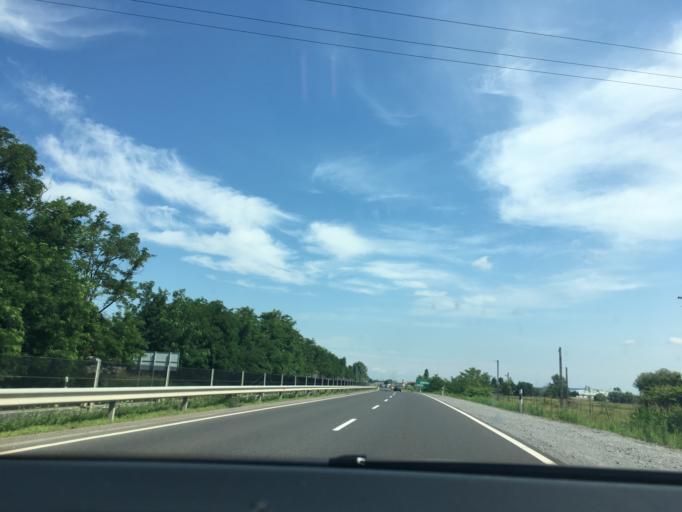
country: HU
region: Szabolcs-Szatmar-Bereg
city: Nyiregyhaza
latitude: 47.8965
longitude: 21.7105
